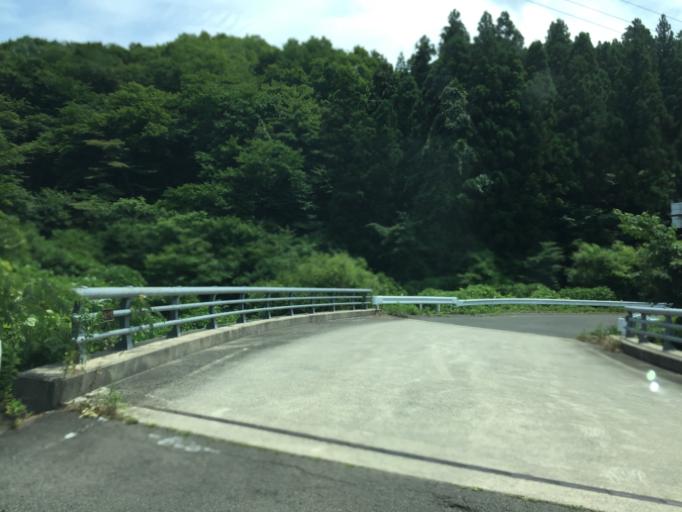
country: JP
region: Fukushima
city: Funehikimachi-funehiki
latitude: 37.6322
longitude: 140.6627
